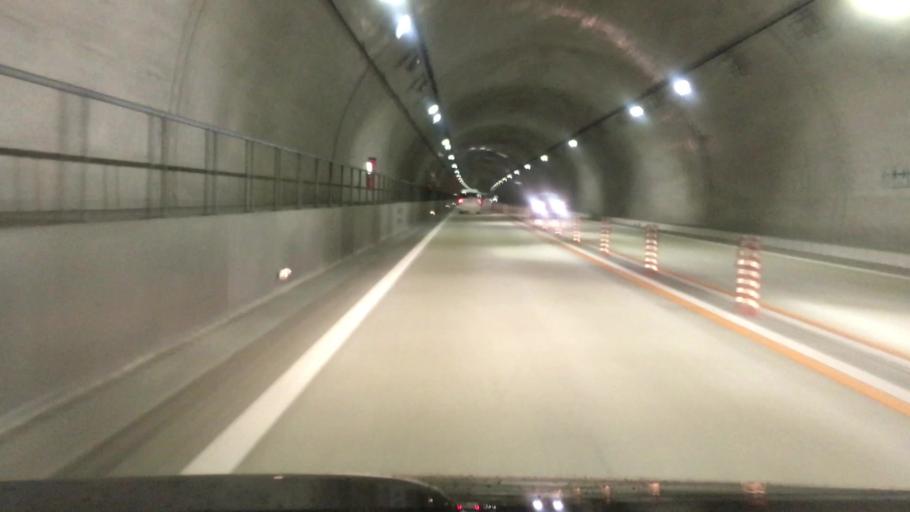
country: JP
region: Hyogo
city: Toyooka
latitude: 35.4512
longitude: 134.7653
